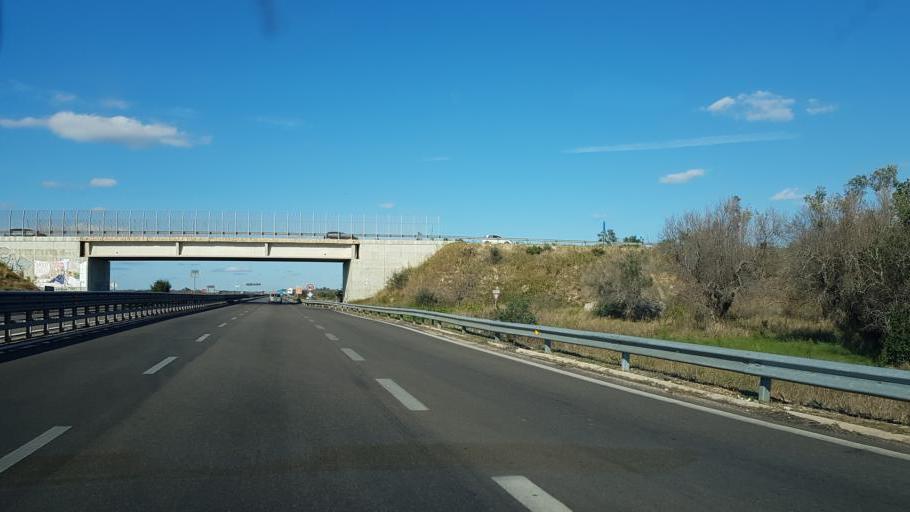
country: IT
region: Apulia
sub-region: Provincia di Lecce
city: Collemeto
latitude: 40.2571
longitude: 18.1185
